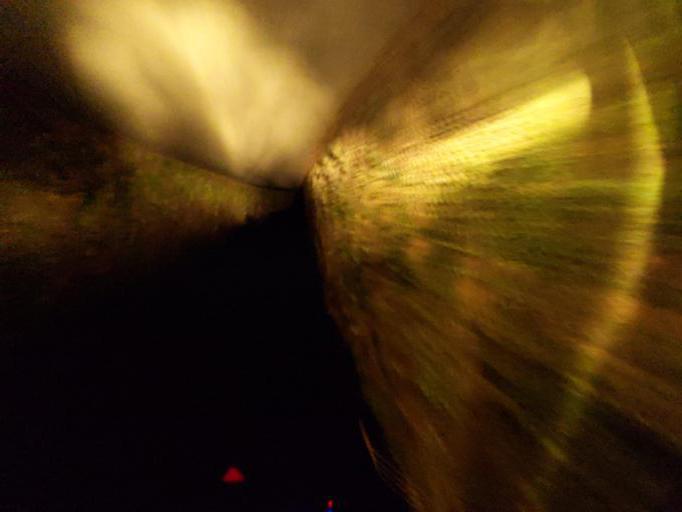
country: GB
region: England
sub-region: Cornwall
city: Torpoint
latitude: 50.3488
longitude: -4.2274
